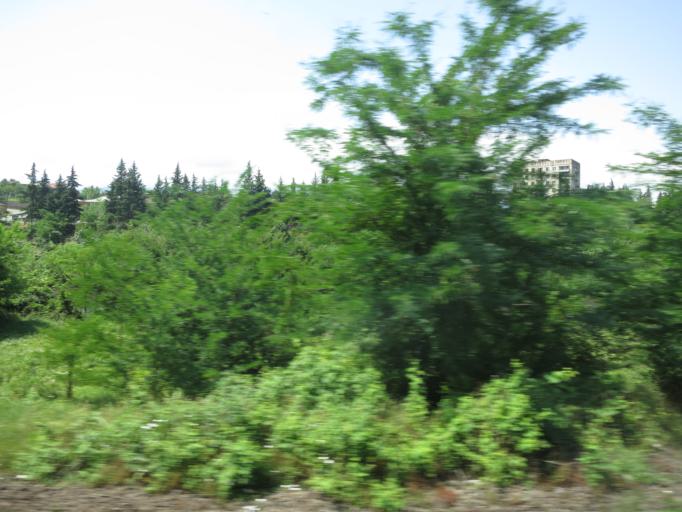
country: GE
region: Imereti
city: Zestap'oni
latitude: 42.1078
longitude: 43.0526
